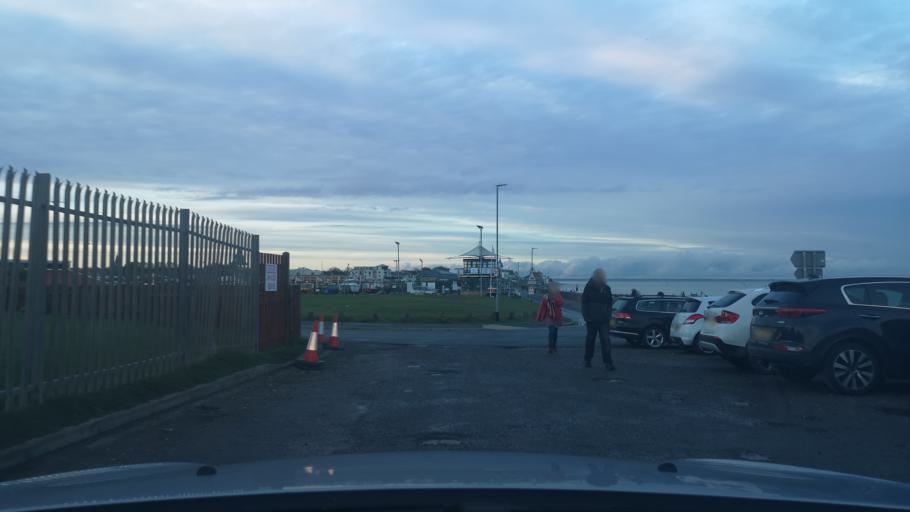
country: GB
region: England
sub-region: East Riding of Yorkshire
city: Hornsea
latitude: 53.9075
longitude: -0.1577
